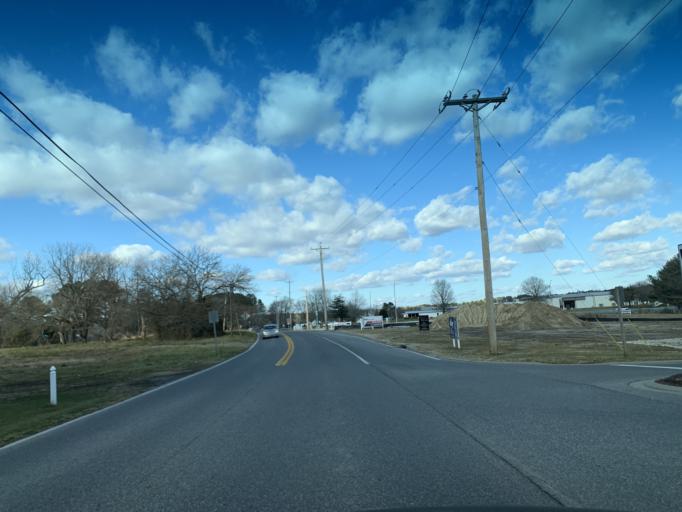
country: US
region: Maryland
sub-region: Worcester County
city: Berlin
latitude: 38.3418
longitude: -75.2194
